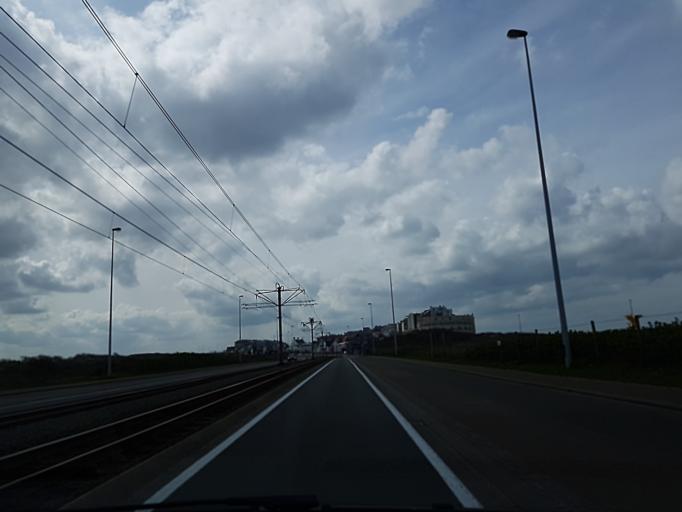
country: BE
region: Flanders
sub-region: Provincie West-Vlaanderen
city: Middelkerke
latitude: 51.1767
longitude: 2.7901
